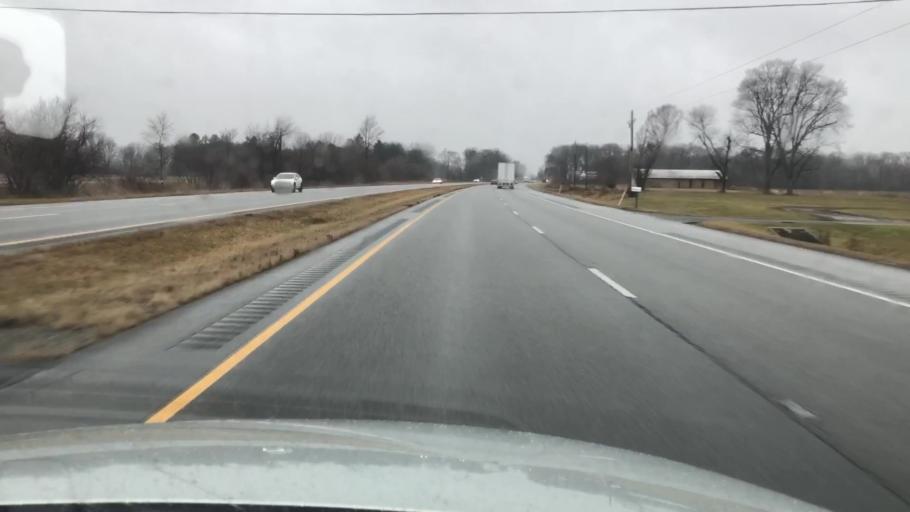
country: US
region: Indiana
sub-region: LaPorte County
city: Wanatah
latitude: 41.4342
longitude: -86.9145
